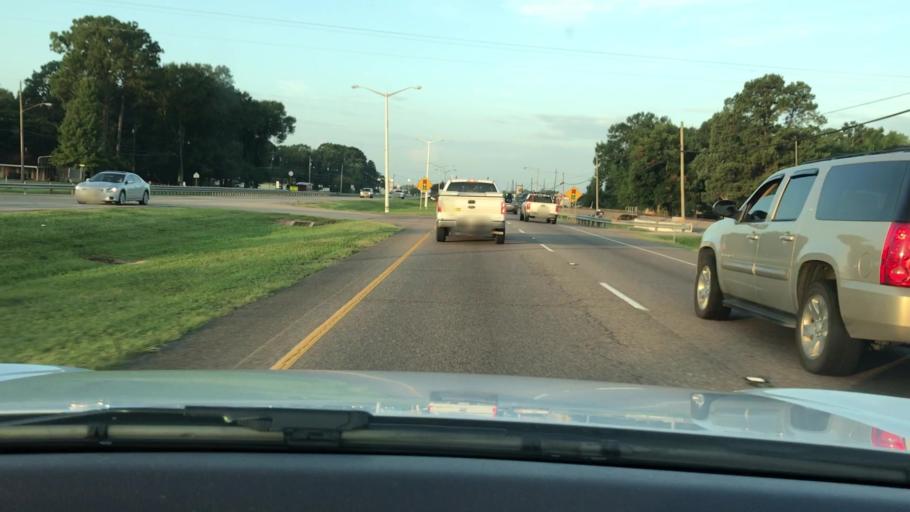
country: US
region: Louisiana
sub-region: West Baton Rouge Parish
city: Brusly
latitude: 30.3927
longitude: -91.2406
